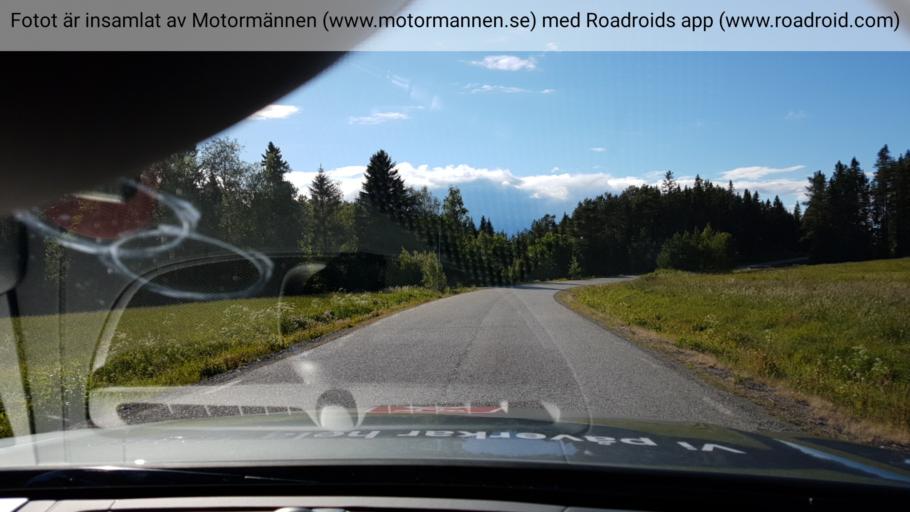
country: SE
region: Jaemtland
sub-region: Bergs Kommun
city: Hoverberg
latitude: 62.9064
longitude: 14.3906
